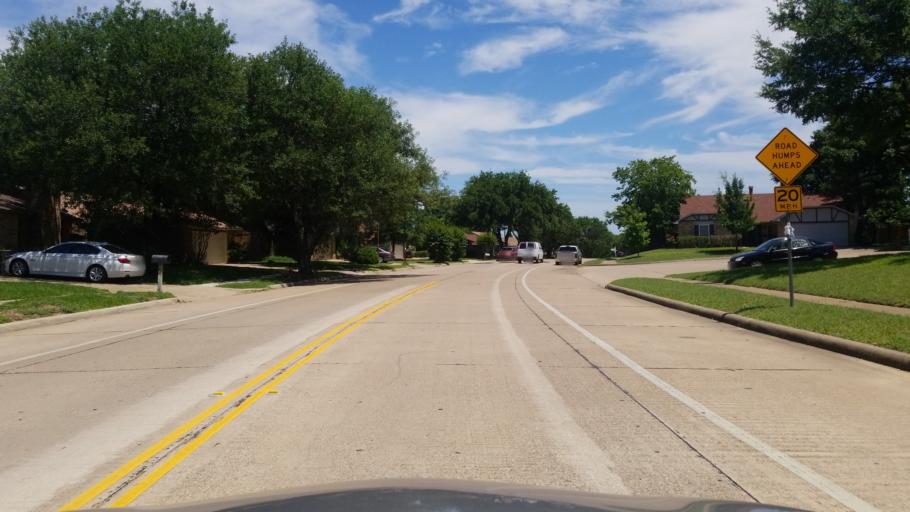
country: US
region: Texas
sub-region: Dallas County
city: Grand Prairie
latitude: 32.6803
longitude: -97.0056
